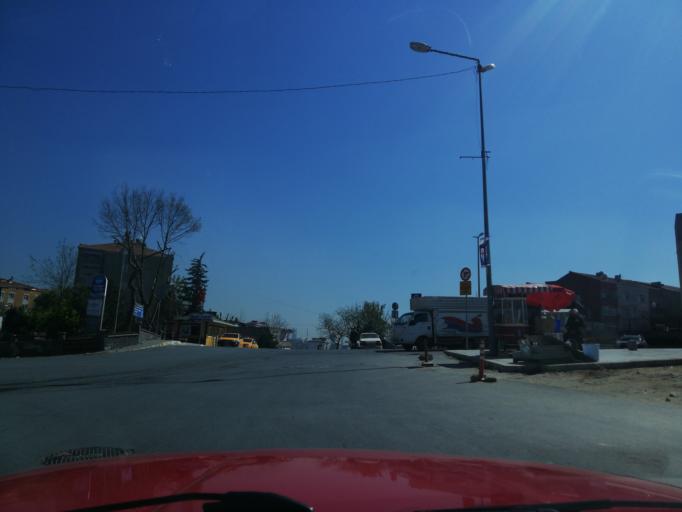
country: TR
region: Istanbul
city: Sisli
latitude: 41.0801
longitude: 28.9376
